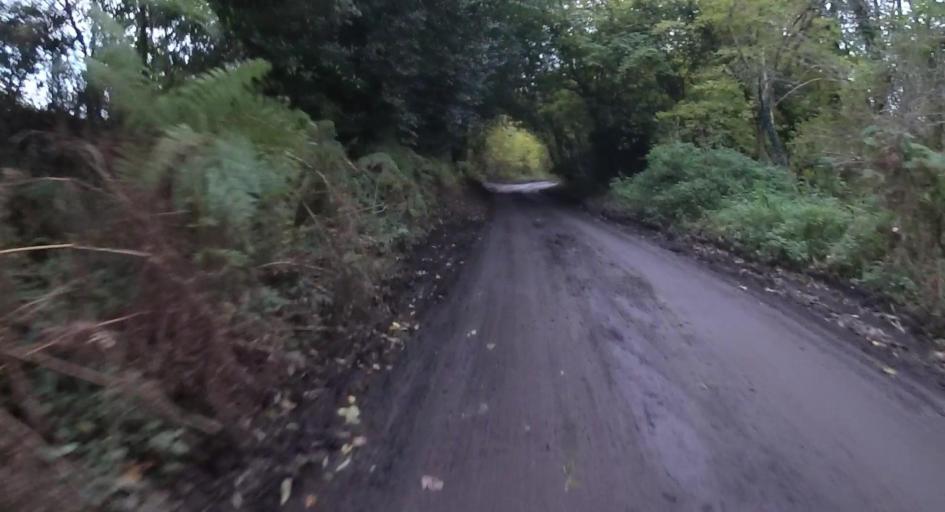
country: GB
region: England
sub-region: Surrey
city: Churt
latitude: 51.1388
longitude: -0.7967
